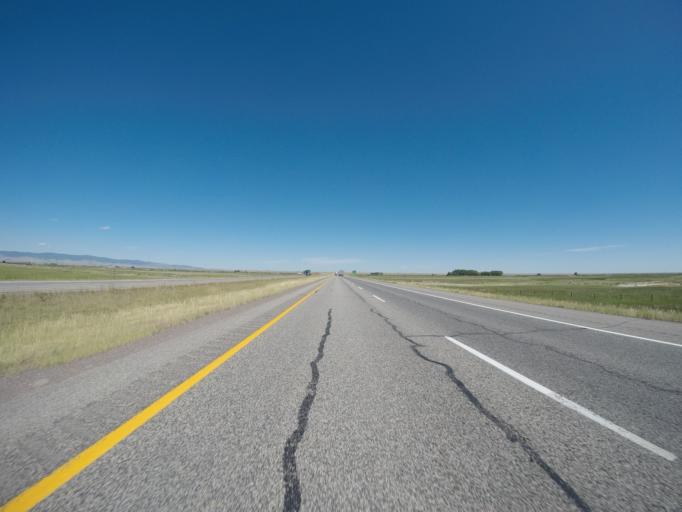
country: US
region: Wyoming
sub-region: Albany County
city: Laramie
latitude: 41.3873
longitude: -105.8176
